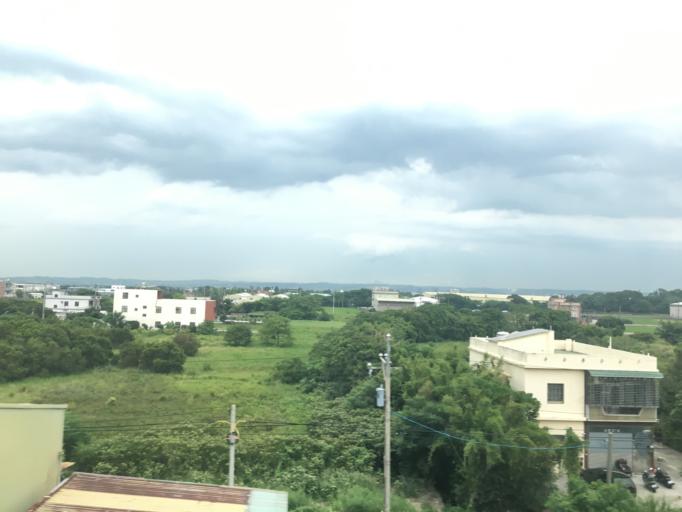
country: TW
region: Taiwan
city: Taoyuan City
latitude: 25.0353
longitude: 121.2164
